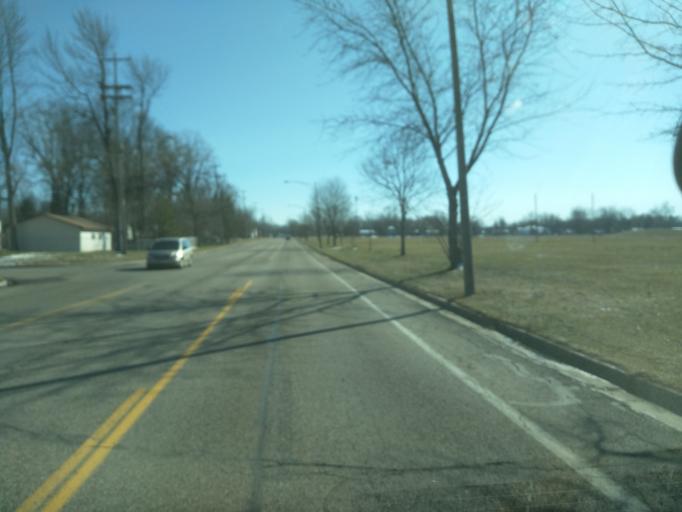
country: US
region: Michigan
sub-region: Ingham County
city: Lansing
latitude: 42.6750
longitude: -84.5874
